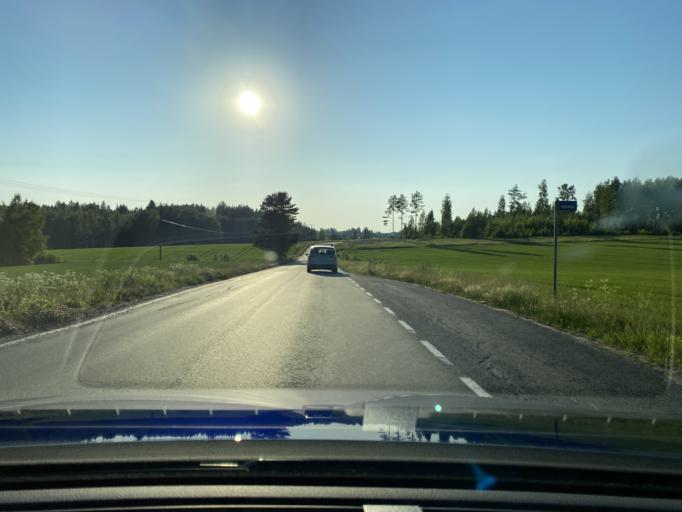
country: FI
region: Haeme
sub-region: Haemeenlinna
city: Tervakoski
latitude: 60.7292
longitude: 24.6772
